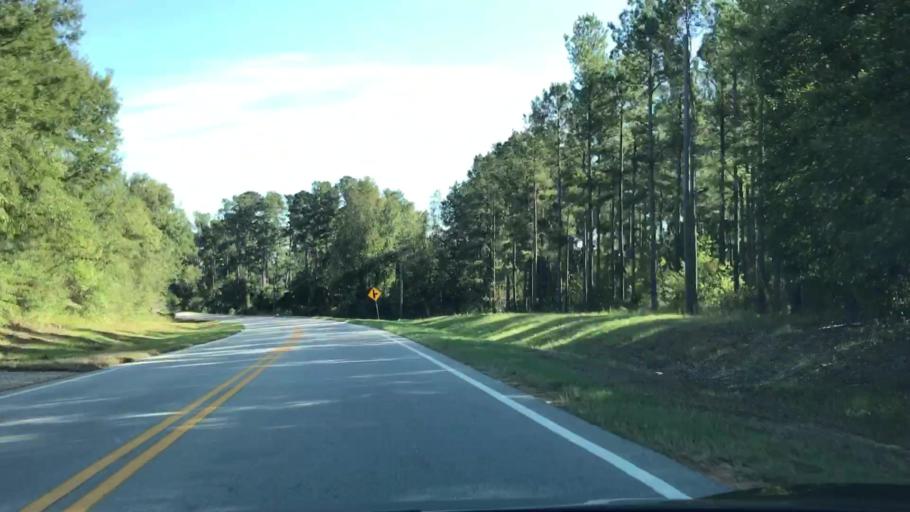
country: US
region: Georgia
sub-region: Glascock County
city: Gibson
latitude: 33.3226
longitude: -82.5584
